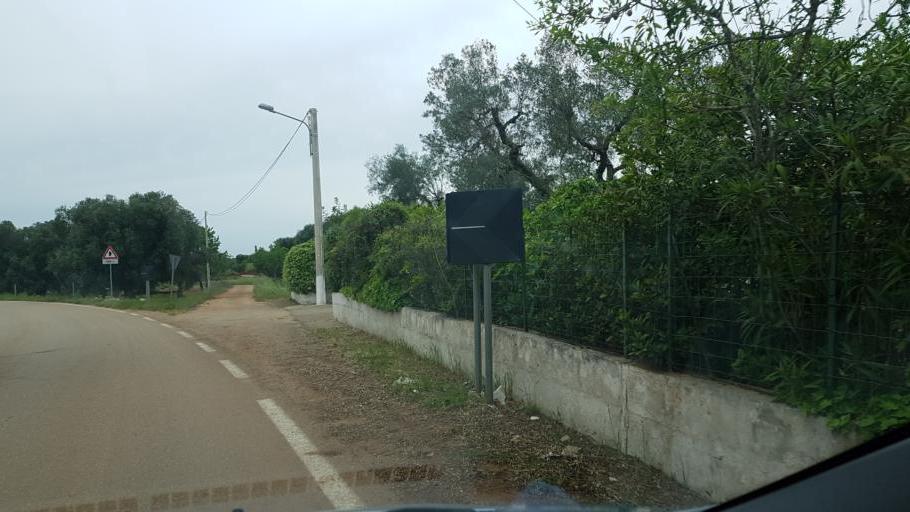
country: IT
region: Apulia
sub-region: Provincia di Brindisi
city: San Vito dei Normanni
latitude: 40.6659
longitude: 17.7447
